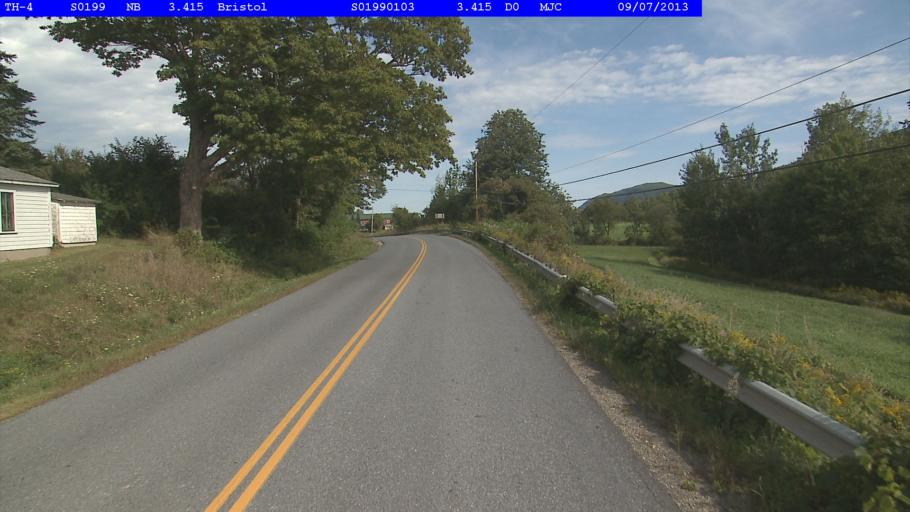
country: US
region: Vermont
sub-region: Addison County
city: Bristol
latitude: 44.1774
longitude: -73.1024
